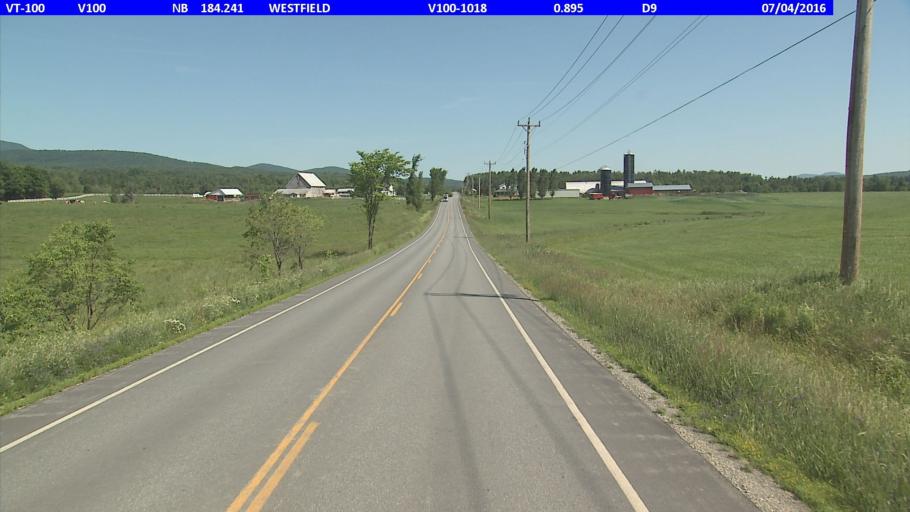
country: US
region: Vermont
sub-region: Orleans County
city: Newport
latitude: 44.8478
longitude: -72.4341
